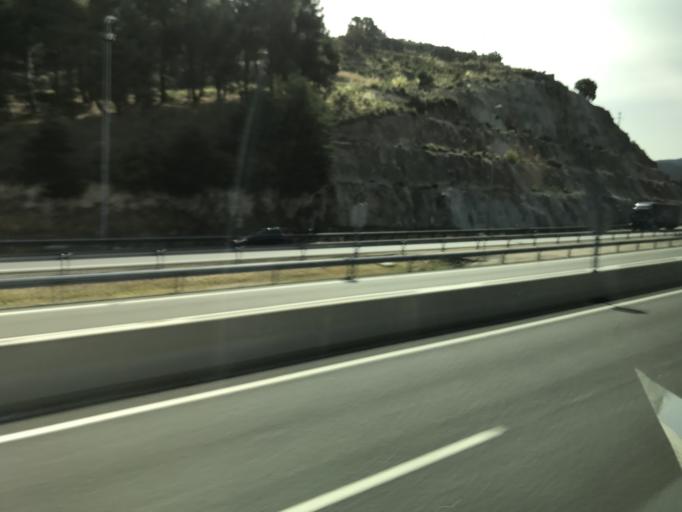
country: ES
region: Castille and Leon
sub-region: Provincia de Avila
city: Peguerinos
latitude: 40.7162
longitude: -4.1870
